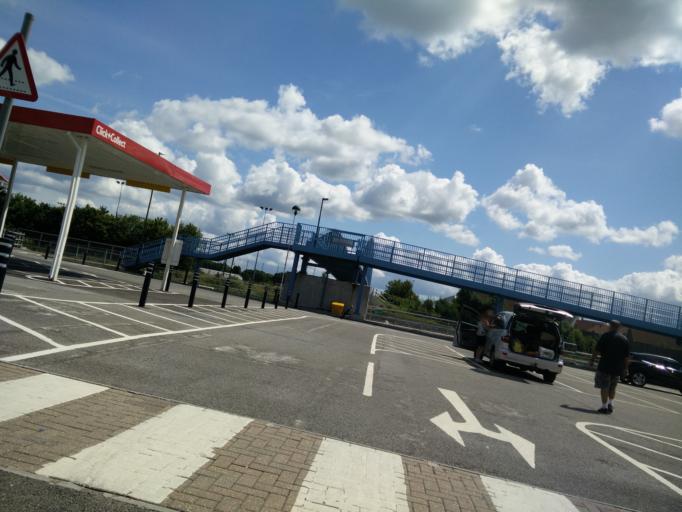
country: GB
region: England
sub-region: West Sussex
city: Horsham
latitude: 51.0653
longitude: -0.3569
